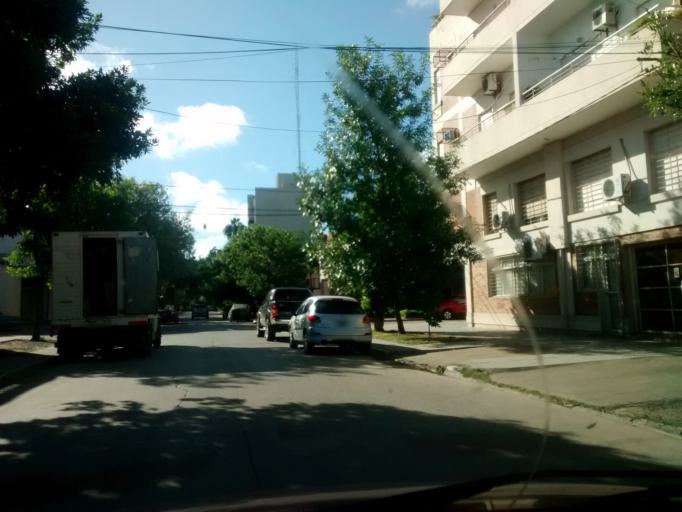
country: AR
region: Chaco
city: Resistencia
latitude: -27.4501
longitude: -58.9754
